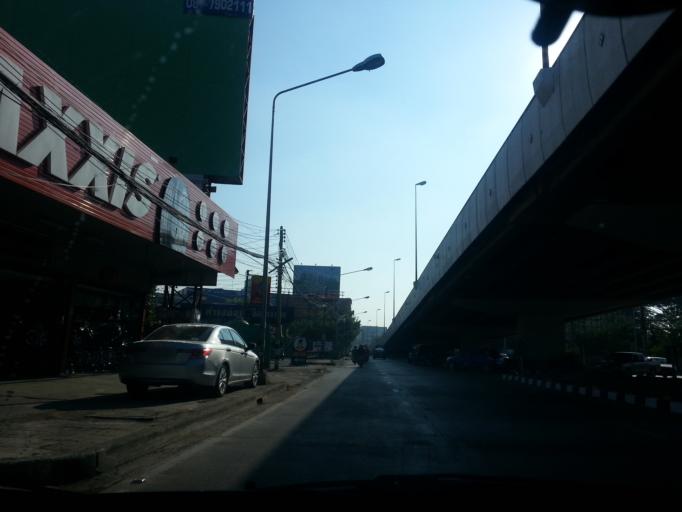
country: TH
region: Chiang Mai
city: Chiang Mai
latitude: 18.7688
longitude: 98.9780
